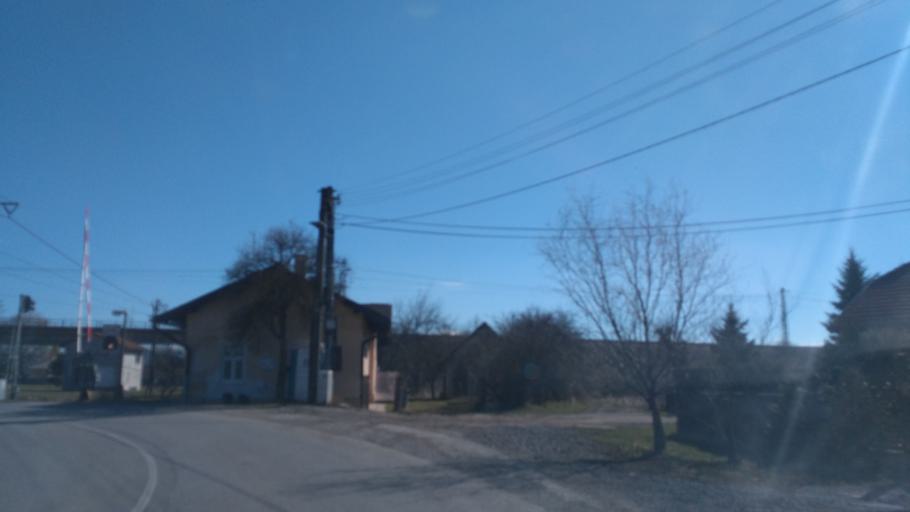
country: SK
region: Kosicky
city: Kosice
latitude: 48.6473
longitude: 21.2873
